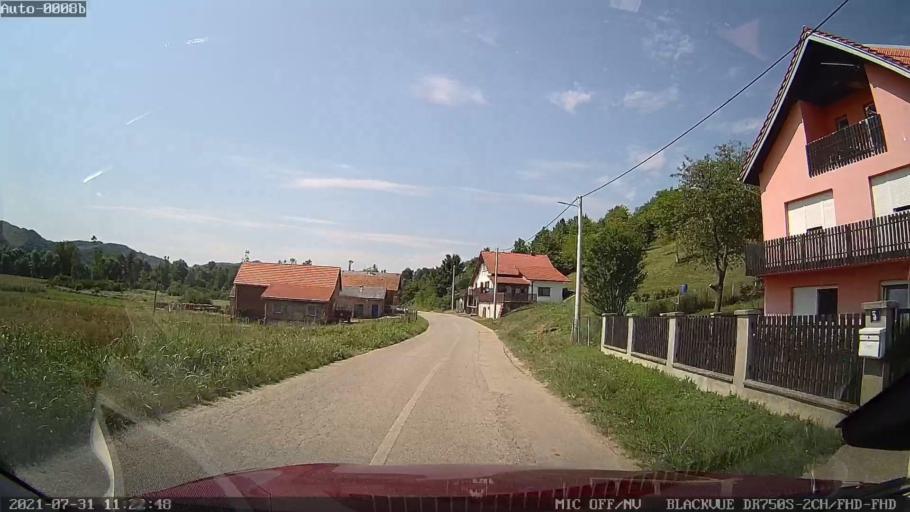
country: HR
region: Varazdinska
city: Jalzabet
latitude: 46.2204
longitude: 16.4661
